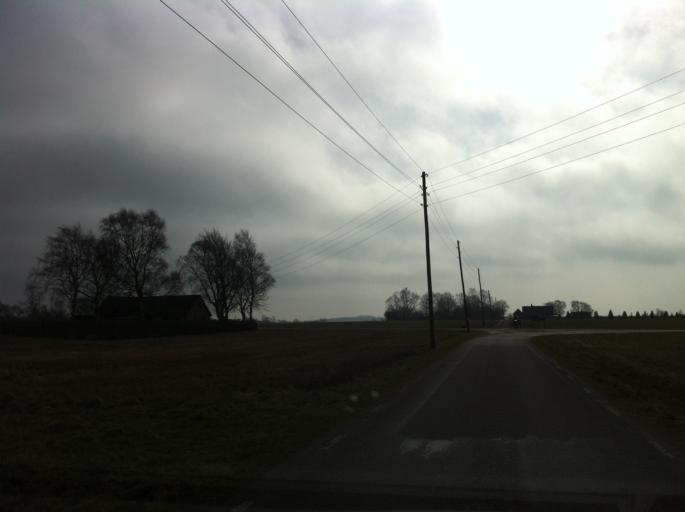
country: SE
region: Skane
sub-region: Svalovs Kommun
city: Teckomatorp
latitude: 55.8654
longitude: 13.0605
